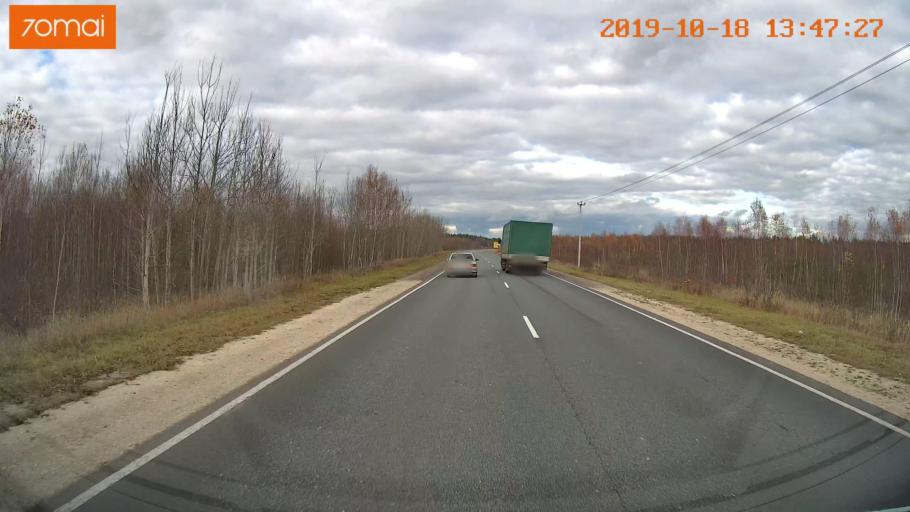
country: RU
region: Moskovskaya
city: Radovitskiy
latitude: 54.9755
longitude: 39.9512
